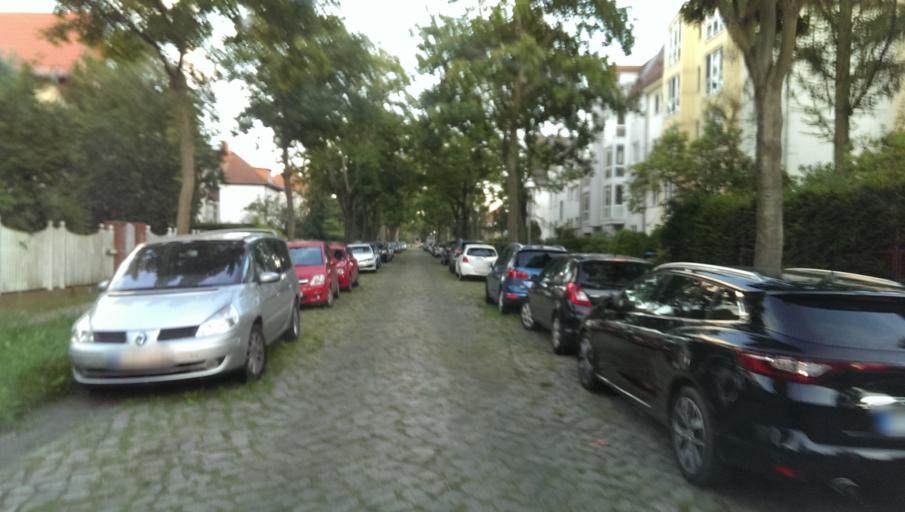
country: DE
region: Berlin
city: Lichterfelde
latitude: 52.4129
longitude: 13.3071
